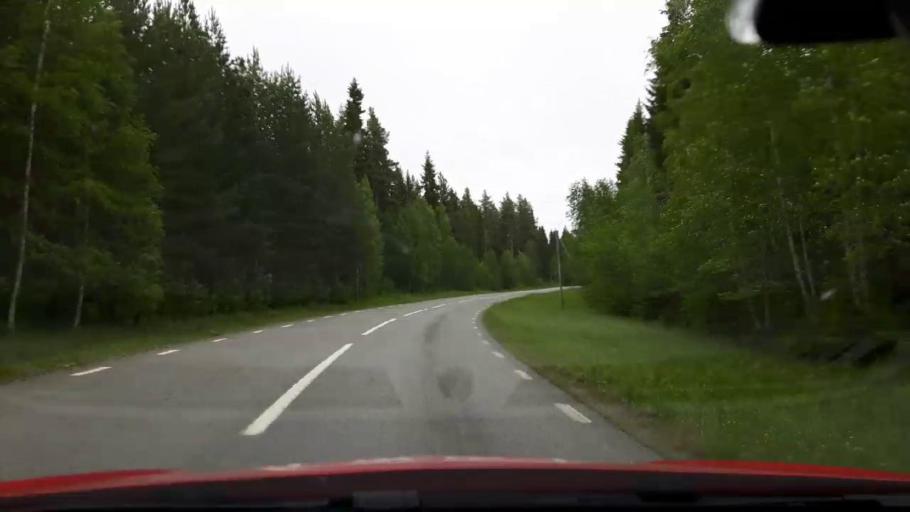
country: SE
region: Jaemtland
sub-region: Stroemsunds Kommun
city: Stroemsund
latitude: 63.3962
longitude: 15.6523
